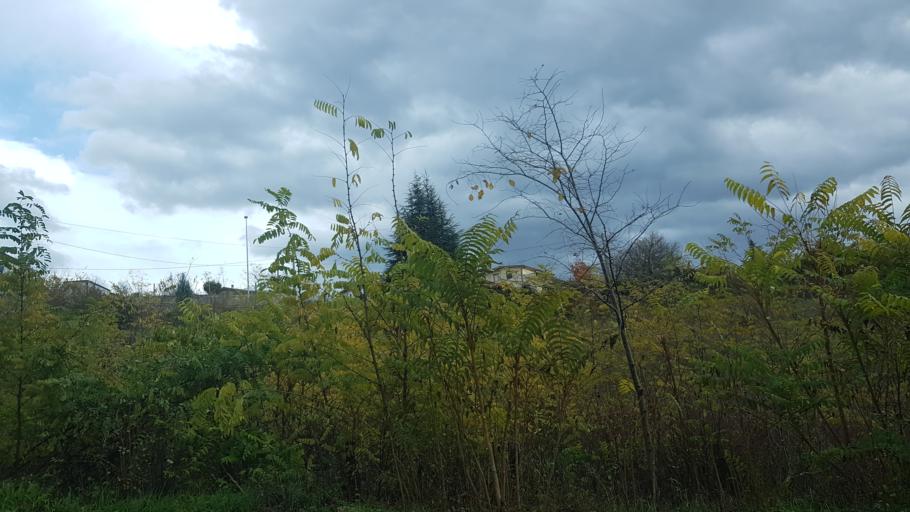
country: IT
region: Abruzzo
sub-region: Provincia dell' Aquila
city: L'Aquila
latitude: 42.3460
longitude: 13.4107
